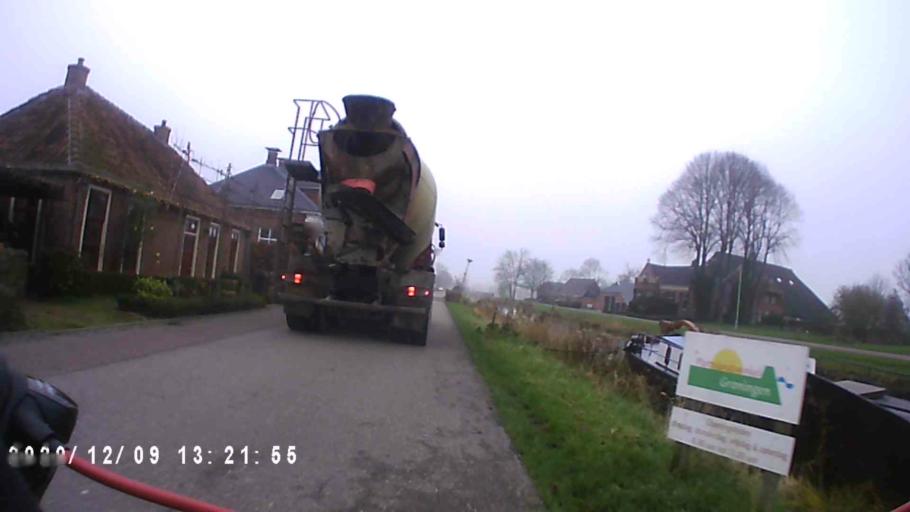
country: NL
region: Groningen
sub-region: Gemeente Bedum
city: Bedum
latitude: 53.2627
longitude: 6.5945
